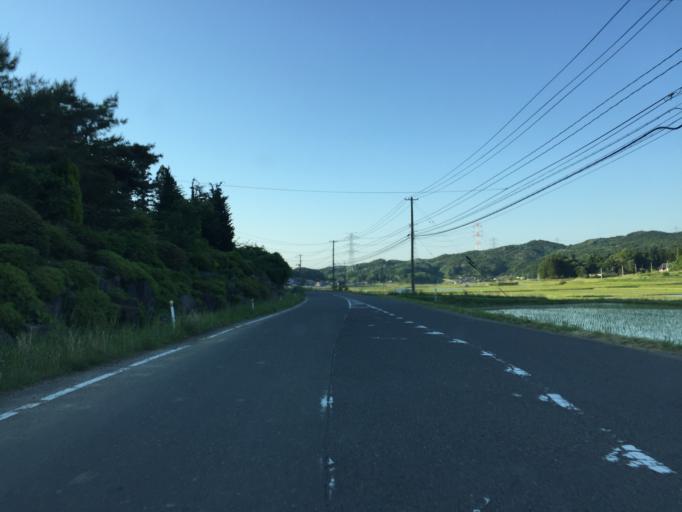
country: JP
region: Fukushima
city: Ishikawa
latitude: 37.0583
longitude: 140.4202
